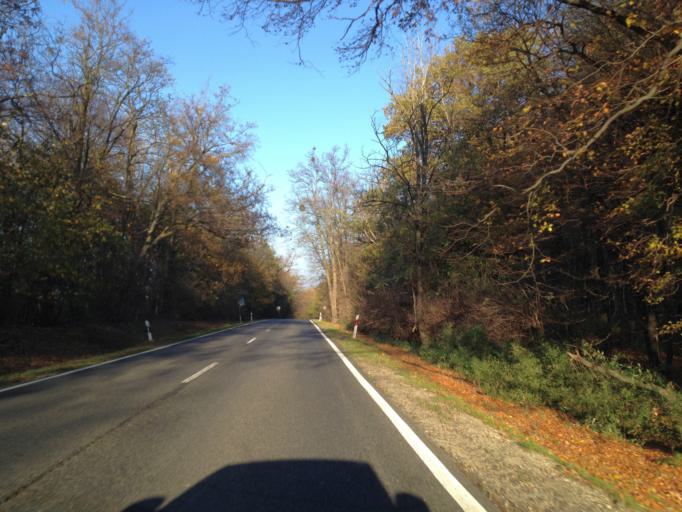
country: HU
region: Veszprem
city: Zirc
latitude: 47.3321
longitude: 17.8825
